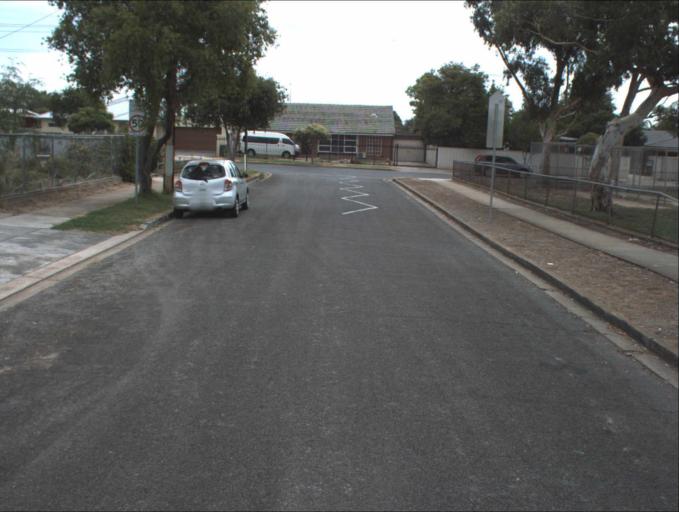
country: AU
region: South Australia
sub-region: Port Adelaide Enfield
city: Enfield
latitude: -34.8500
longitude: 138.6193
